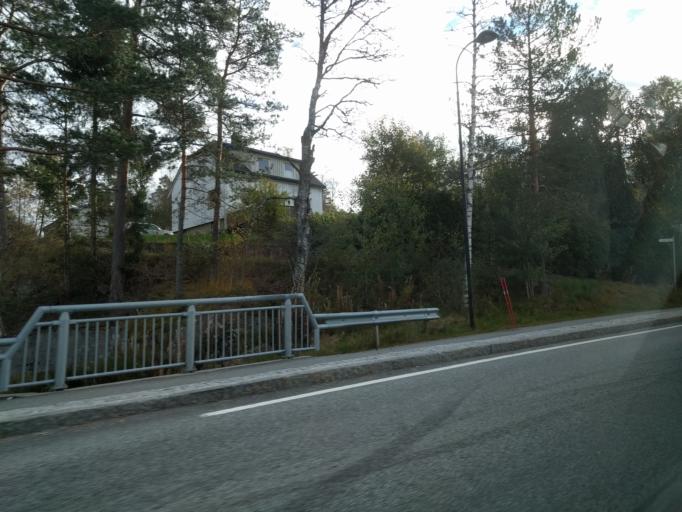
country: NO
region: Vest-Agder
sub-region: Songdalen
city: Nodeland
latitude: 58.2644
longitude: 7.8304
